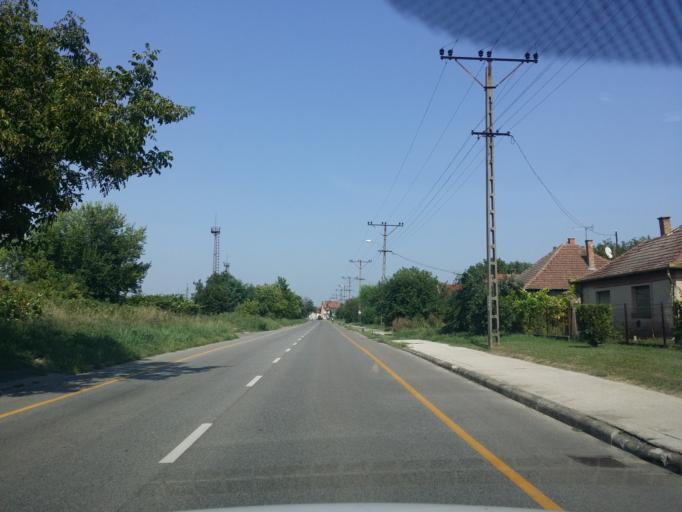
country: HU
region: Tolna
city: Simontornya
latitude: 46.7534
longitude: 18.5375
